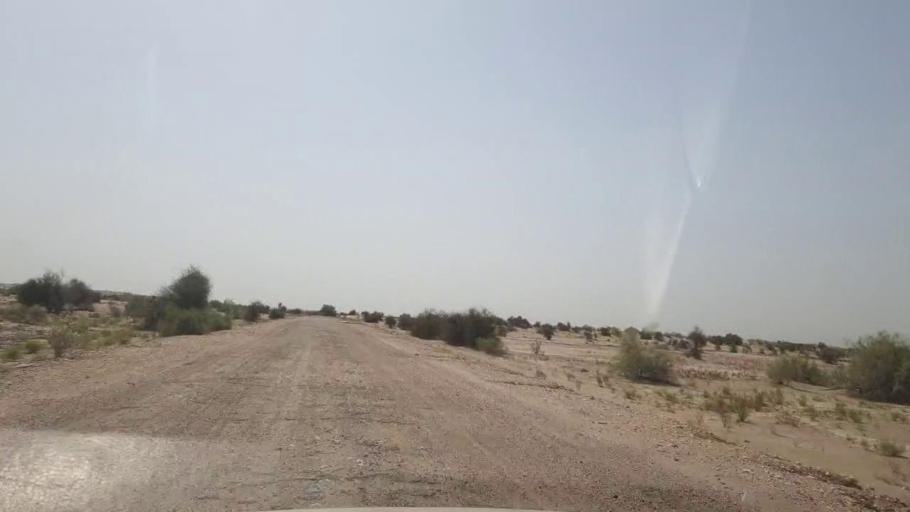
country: PK
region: Sindh
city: Khanpur
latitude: 27.4302
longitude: 69.2552
